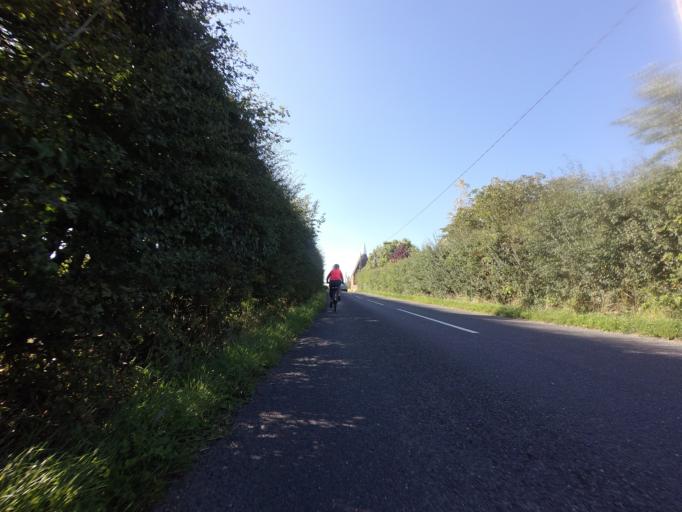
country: GB
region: England
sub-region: Kent
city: Tenterden
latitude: 51.0521
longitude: 0.6934
